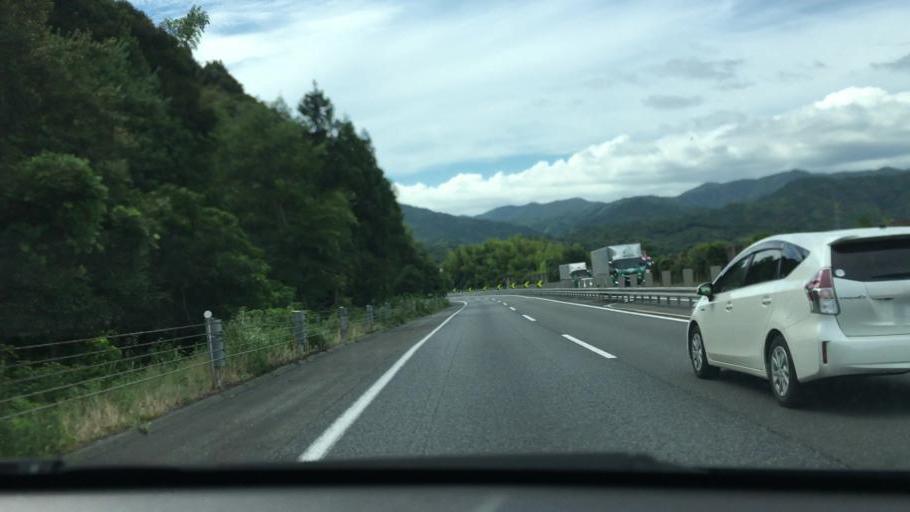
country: JP
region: Yamaguchi
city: Ogori-shimogo
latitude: 34.1308
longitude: 131.4342
